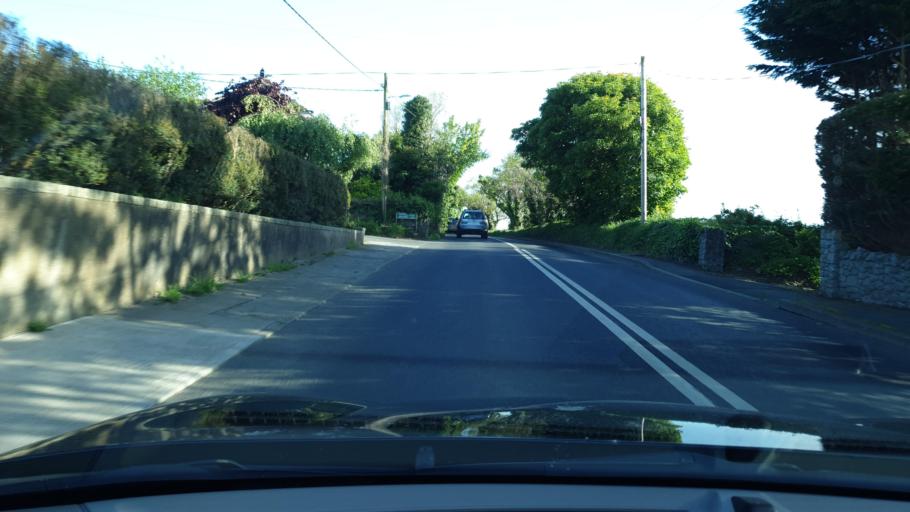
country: IE
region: Leinster
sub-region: Fingal County
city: Skerries
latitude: 53.5616
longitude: -6.1037
